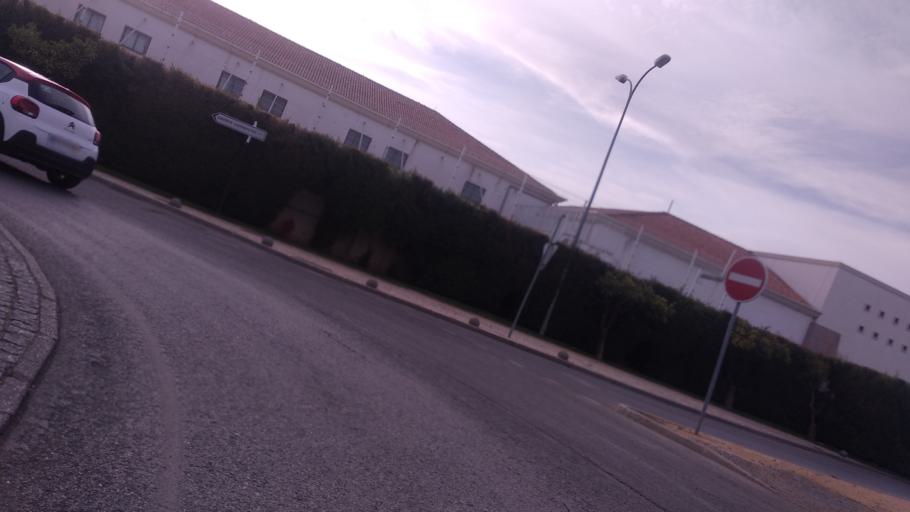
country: PT
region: Faro
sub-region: Faro
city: Faro
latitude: 37.0296
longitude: -7.9433
